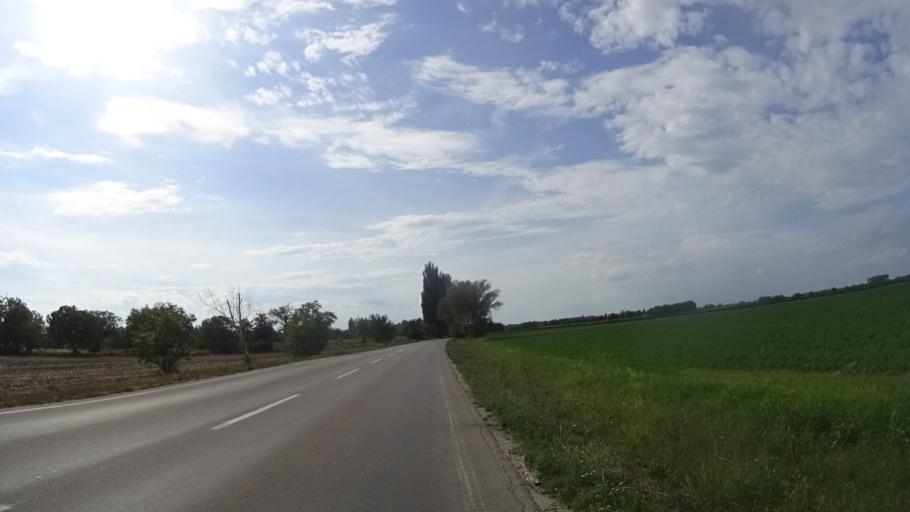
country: SK
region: Trnavsky
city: Gabcikovo
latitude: 47.9137
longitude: 17.5118
